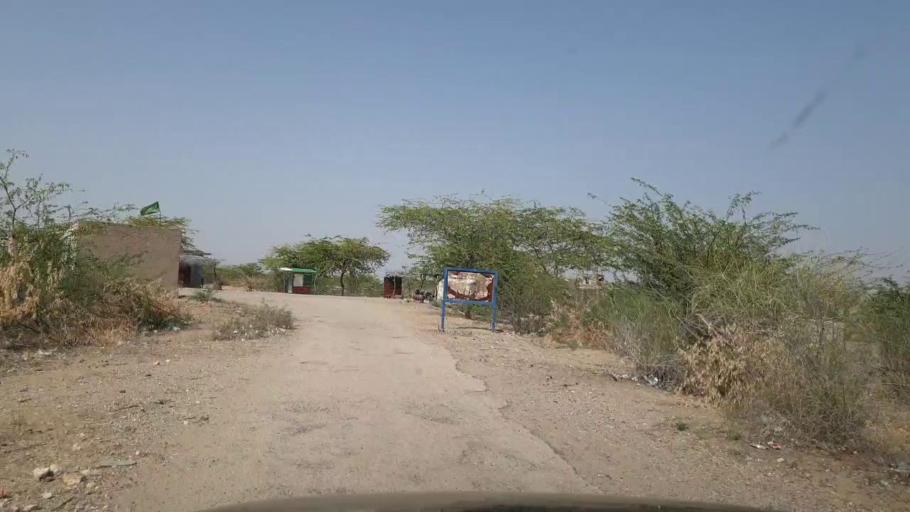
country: PK
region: Sindh
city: Islamkot
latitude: 25.0606
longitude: 70.4495
